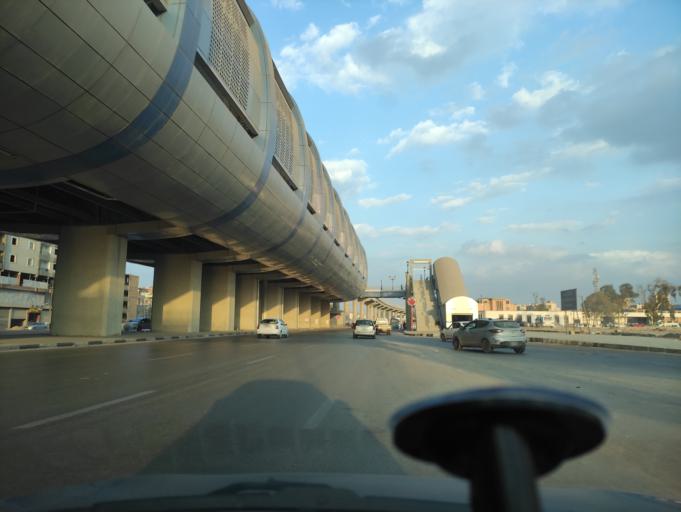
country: EG
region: Muhafazat al Qalyubiyah
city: Al Khankah
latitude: 30.1279
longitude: 31.3600
